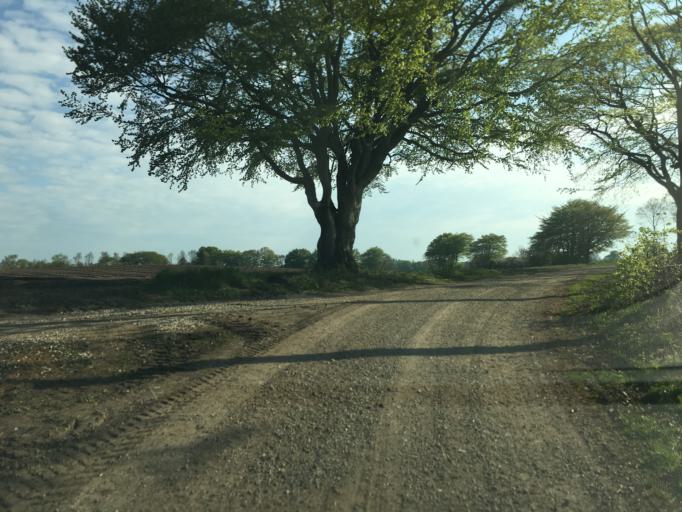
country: DK
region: South Denmark
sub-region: Aabenraa Kommune
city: Rodekro
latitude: 55.1557
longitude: 9.3839
